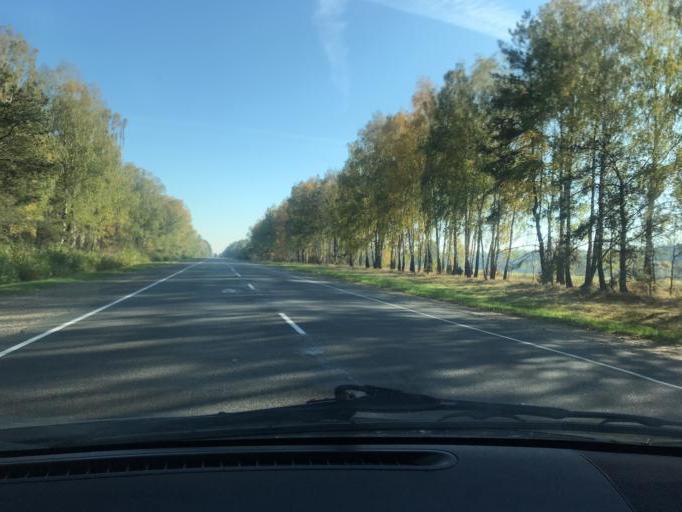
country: BY
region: Brest
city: Ivanava
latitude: 52.1546
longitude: 25.5809
